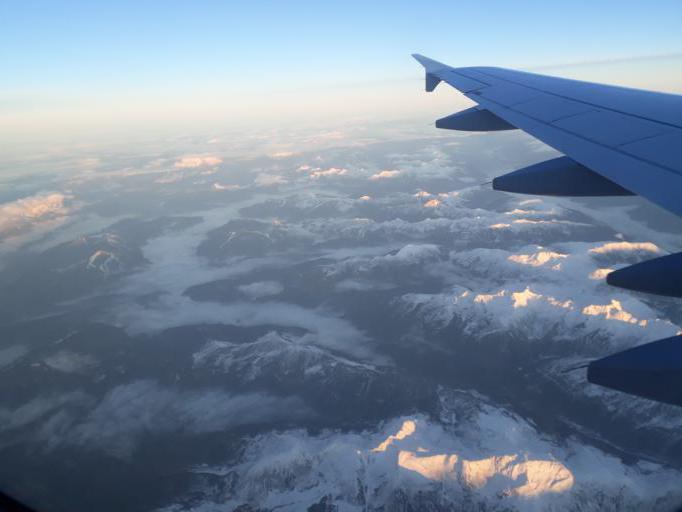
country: AT
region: Tyrol
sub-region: Politischer Bezirk Schwaz
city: Stummerberg
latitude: 47.3349
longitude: 11.9204
